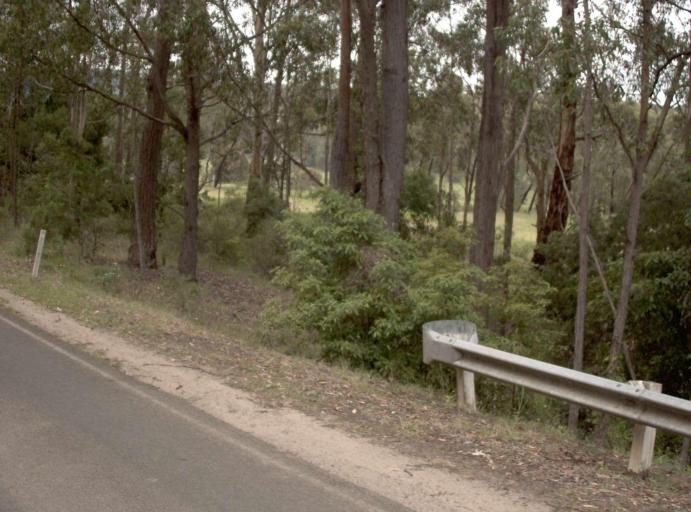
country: AU
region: Victoria
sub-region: Latrobe
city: Traralgon
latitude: -38.4906
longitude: 146.6407
